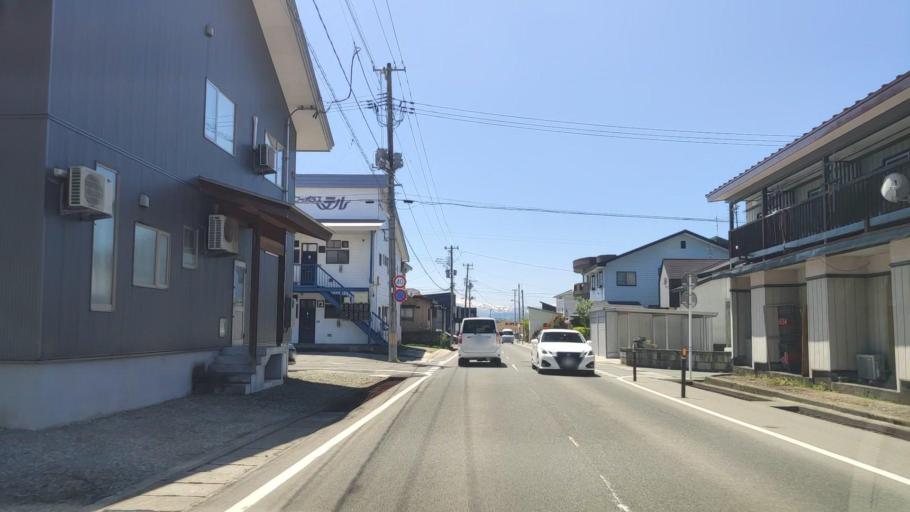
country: JP
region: Yamagata
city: Shinjo
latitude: 38.7578
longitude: 140.2977
